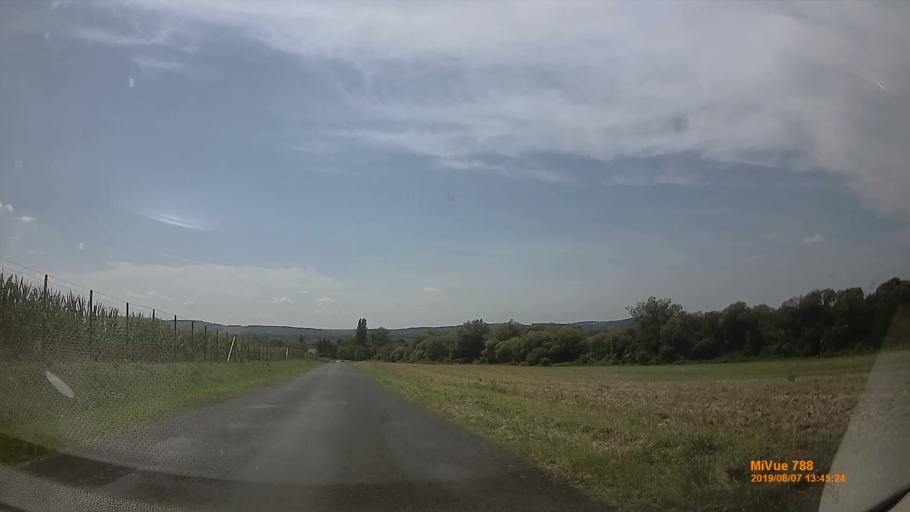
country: HU
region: Zala
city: Cserszegtomaj
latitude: 46.8844
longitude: 17.2032
